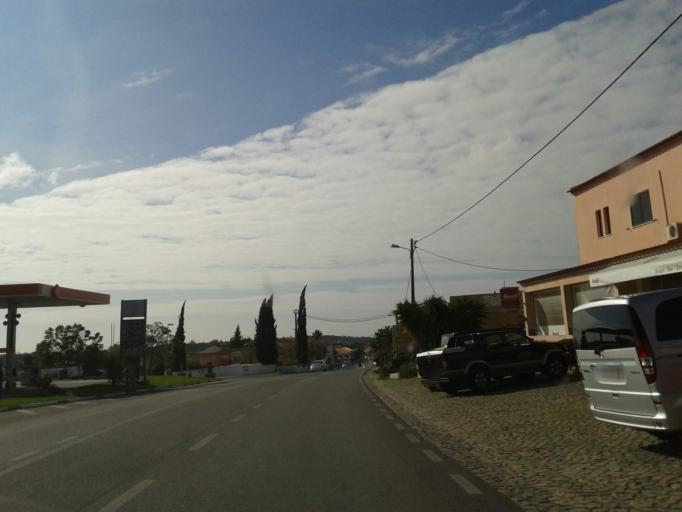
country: PT
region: Faro
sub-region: Loule
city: Almancil
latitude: 37.0857
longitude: -8.0423
